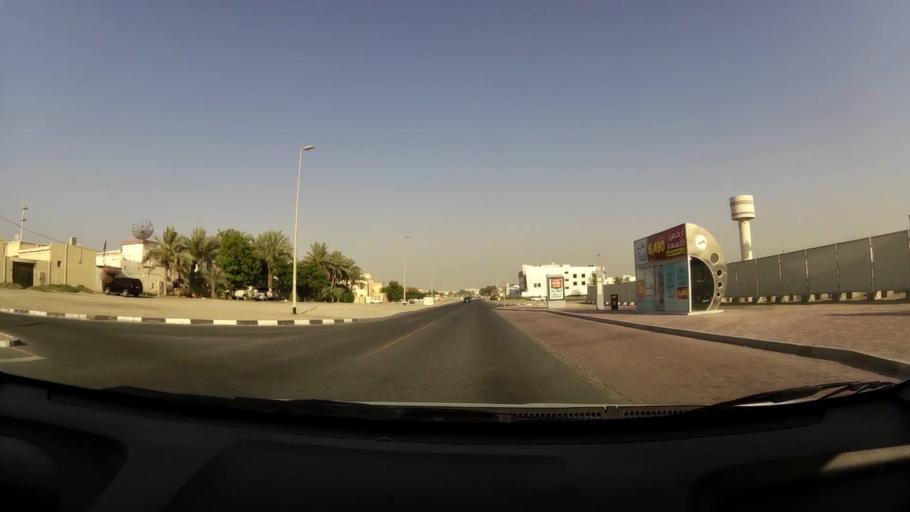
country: AE
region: Ash Shariqah
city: Sharjah
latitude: 25.2678
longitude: 55.3897
